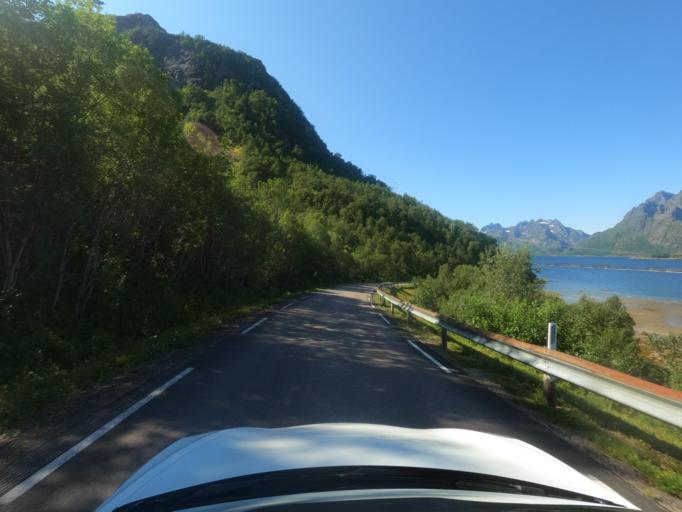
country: NO
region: Nordland
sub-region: Hadsel
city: Stokmarknes
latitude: 68.3394
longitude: 15.0463
